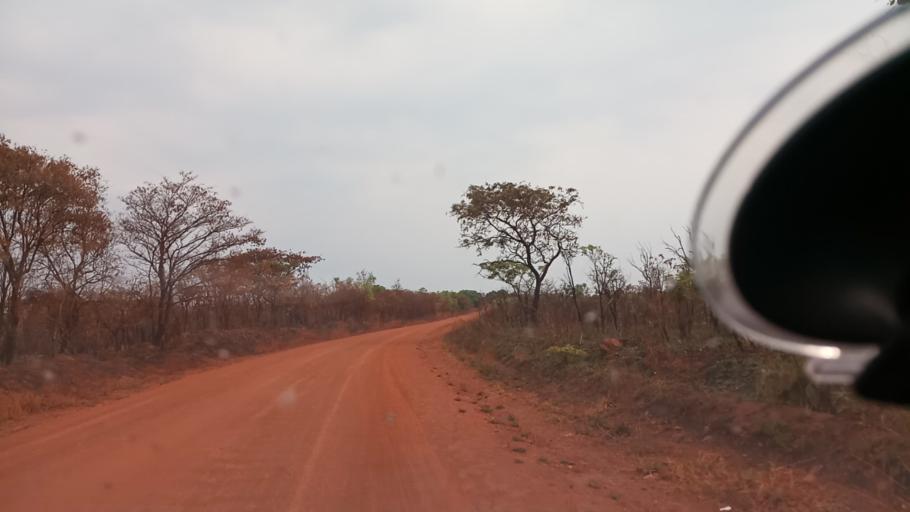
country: ZM
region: Luapula
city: Nchelenge
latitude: -9.1715
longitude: 28.2812
